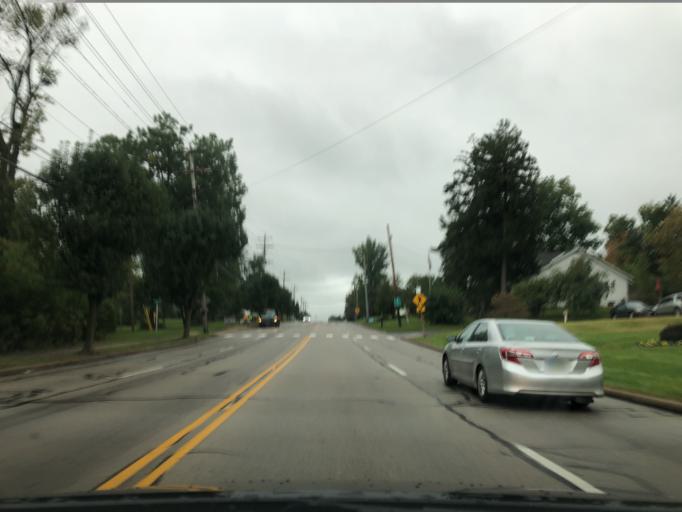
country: US
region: Ohio
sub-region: Hamilton County
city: Rossmoyne
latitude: 39.2099
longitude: -84.3793
